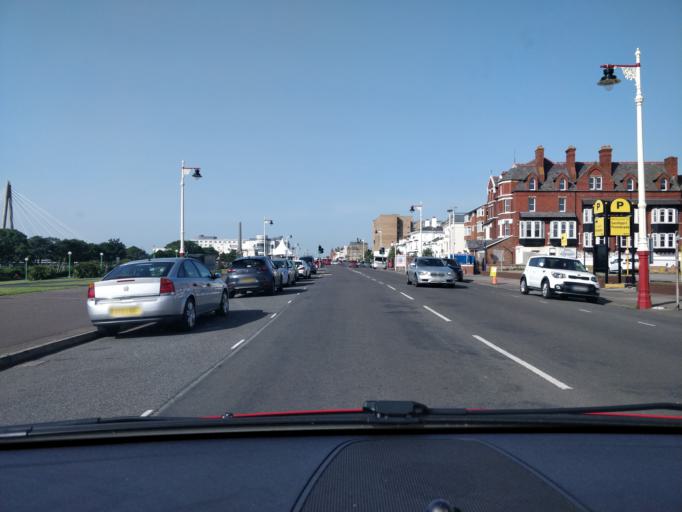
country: GB
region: England
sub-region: Sefton
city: Southport
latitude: 53.6479
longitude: -3.0102
